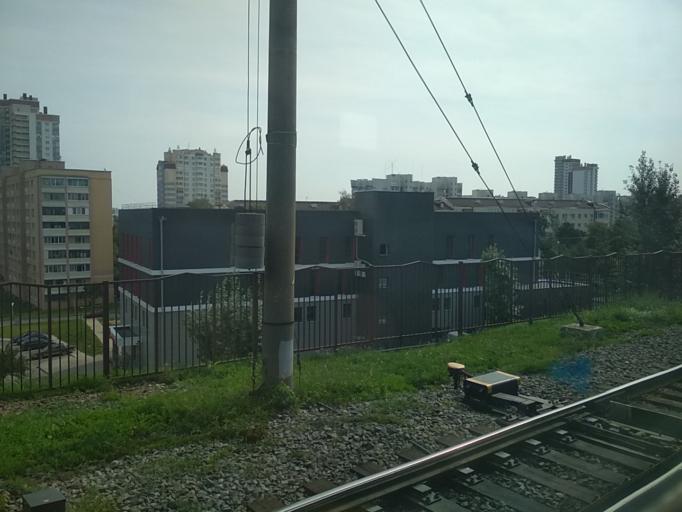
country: BY
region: Minsk
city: Minsk
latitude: 53.8838
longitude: 27.5635
